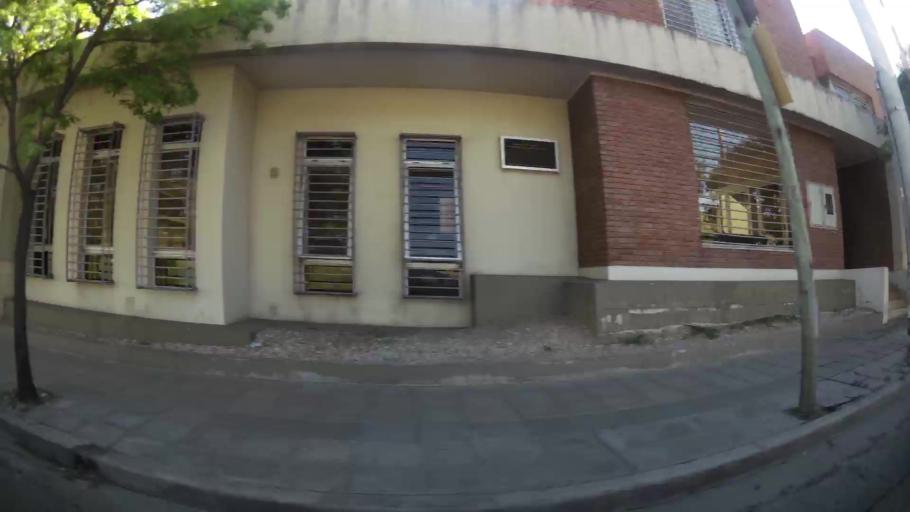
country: AR
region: Cordoba
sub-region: Departamento de Capital
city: Cordoba
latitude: -31.4264
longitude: -64.1698
